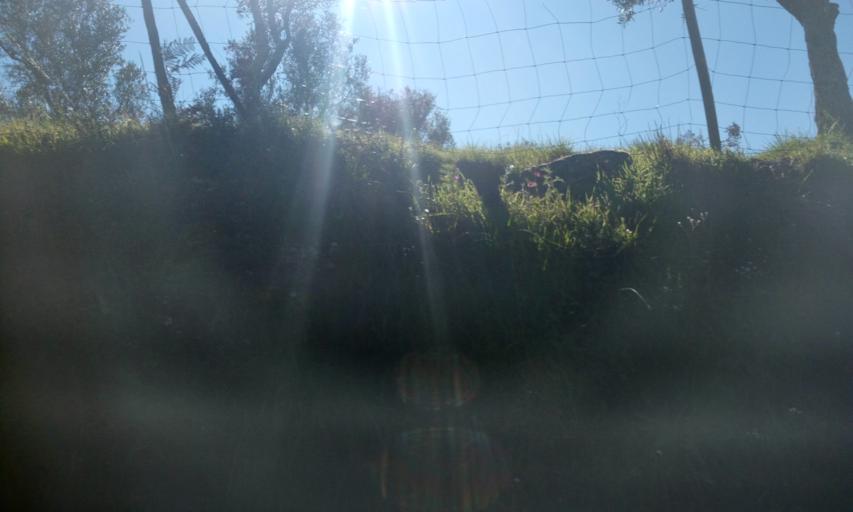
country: PT
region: Guarda
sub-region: Fornos de Algodres
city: Fornos de Algodres
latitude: 40.5250
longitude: -7.5567
